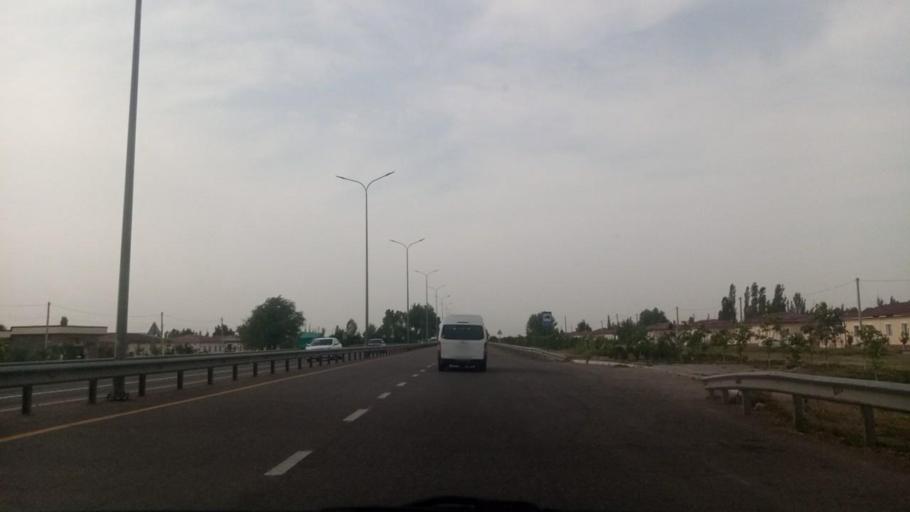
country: UZ
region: Toshkent
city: Tuytepa
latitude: 41.1311
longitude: 69.4363
